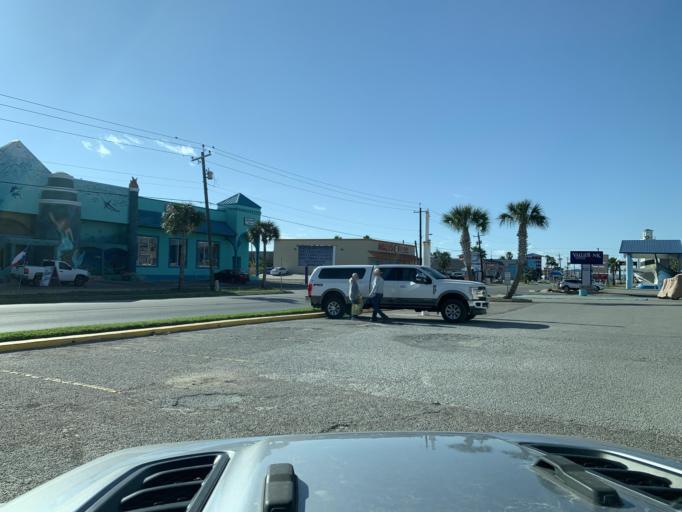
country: US
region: Texas
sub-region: Nueces County
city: Port Aransas
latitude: 27.8302
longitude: -97.0655
